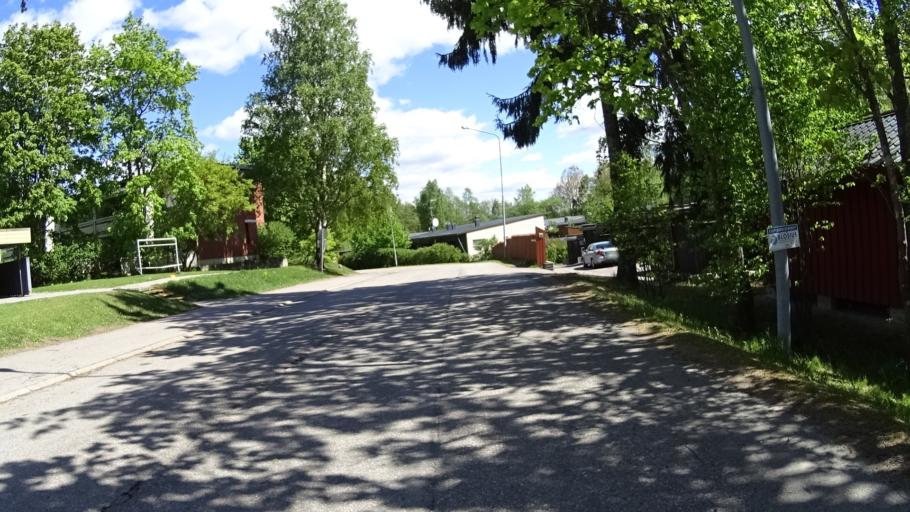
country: FI
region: Uusimaa
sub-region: Helsinki
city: Kauniainen
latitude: 60.2260
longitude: 24.7096
